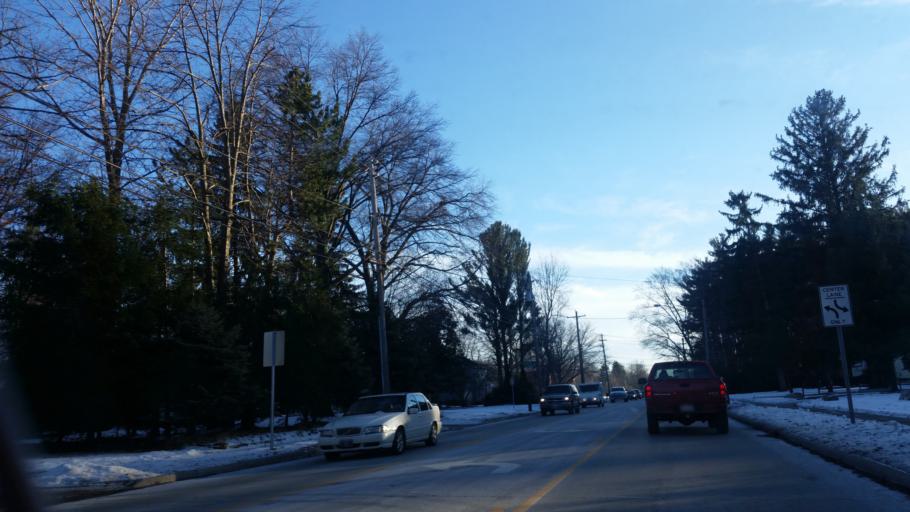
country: US
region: Ohio
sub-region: Cuyahoga County
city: Fairview Park
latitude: 41.4688
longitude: -81.8826
